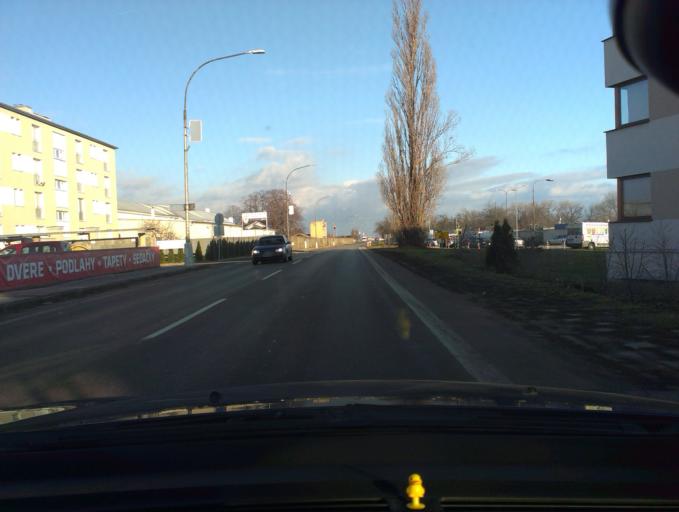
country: SK
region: Trnavsky
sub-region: Okres Trnava
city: Piestany
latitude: 48.6072
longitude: 17.8328
